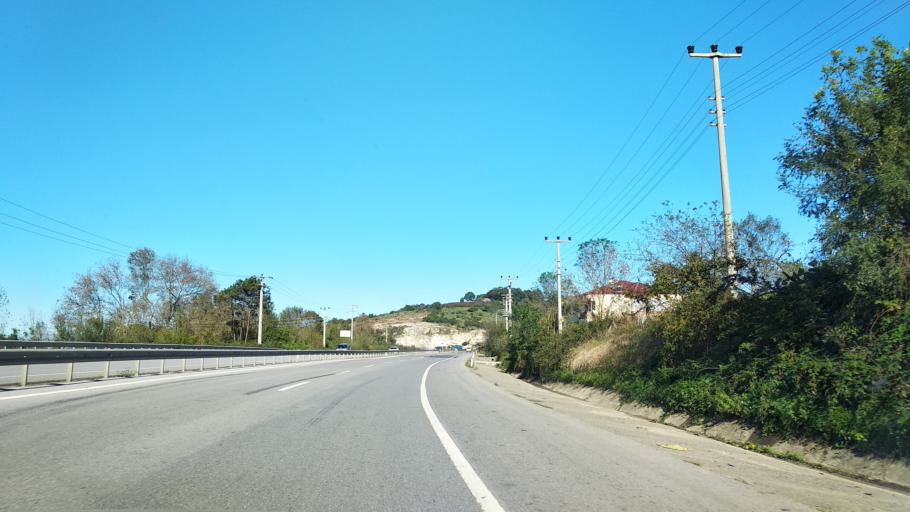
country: TR
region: Sakarya
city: Karasu
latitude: 41.0903
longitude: 30.6486
